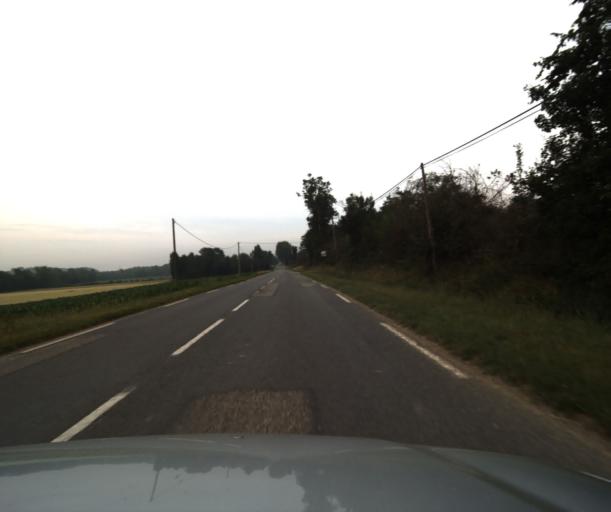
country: FR
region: Midi-Pyrenees
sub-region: Departement du Tarn-et-Garonne
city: Beaumont-de-Lomagne
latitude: 43.8138
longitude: 0.9042
